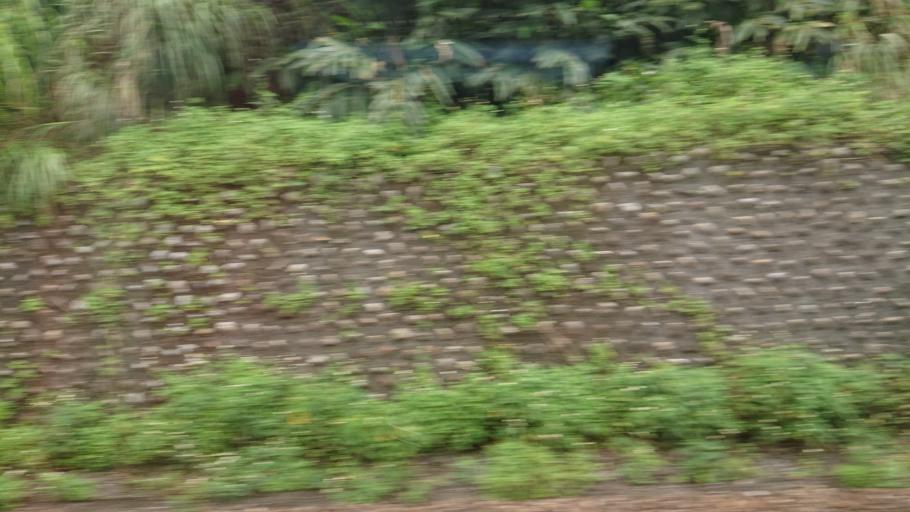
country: TW
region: Taiwan
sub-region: Yilan
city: Yilan
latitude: 24.9212
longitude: 121.8829
